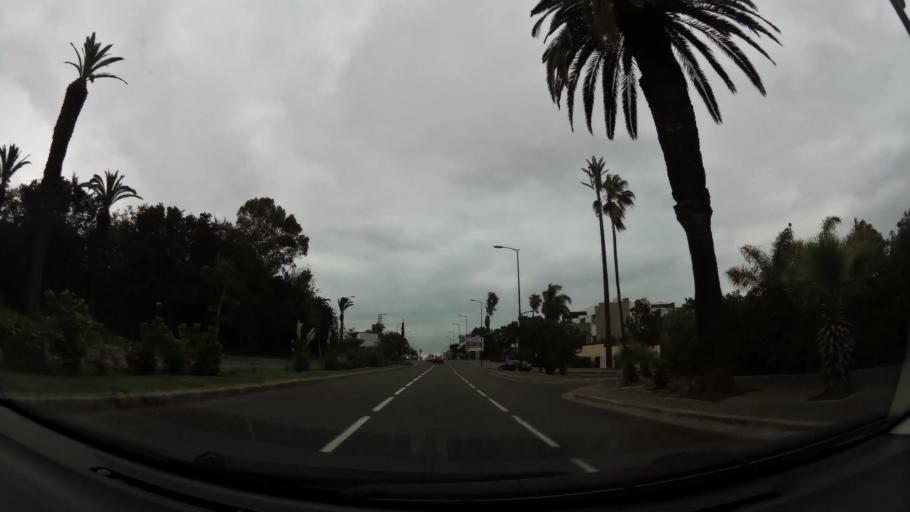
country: MA
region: Grand Casablanca
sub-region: Casablanca
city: Casablanca
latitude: 33.5919
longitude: -7.6585
